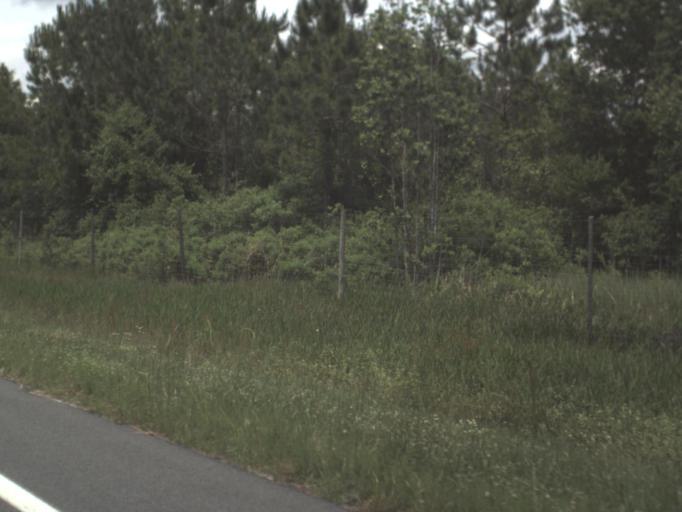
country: US
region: Florida
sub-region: Columbia County
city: Five Points
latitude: 30.4902
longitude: -82.6621
